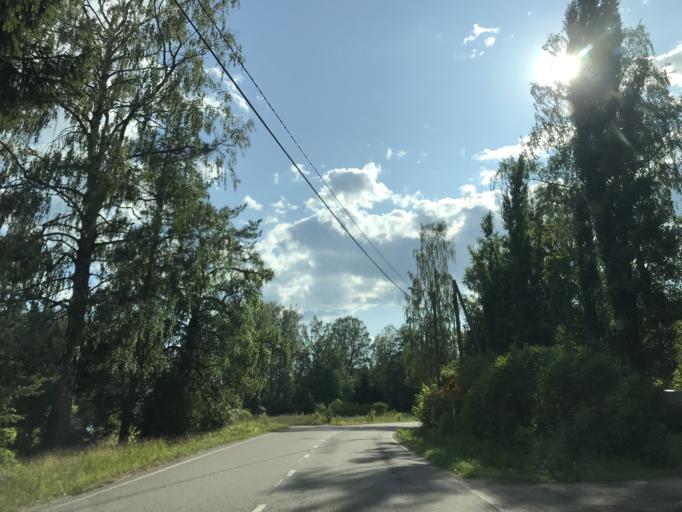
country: FI
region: Uusimaa
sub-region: Helsinki
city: Nurmijaervi
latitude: 60.4502
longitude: 24.5796
